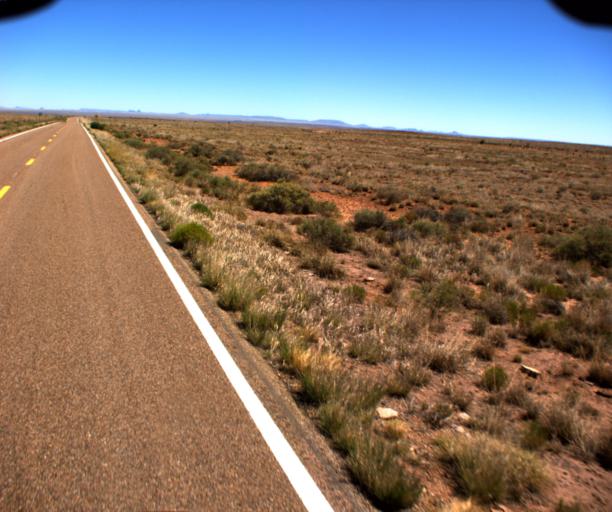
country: US
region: Arizona
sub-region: Navajo County
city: Winslow
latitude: 34.8921
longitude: -110.6472
